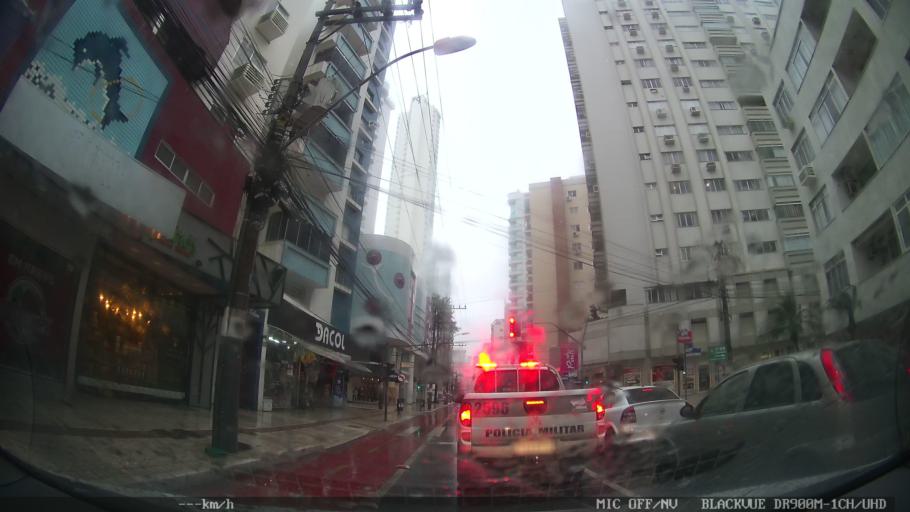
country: BR
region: Santa Catarina
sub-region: Balneario Camboriu
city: Balneario Camboriu
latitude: -26.9802
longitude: -48.6366
